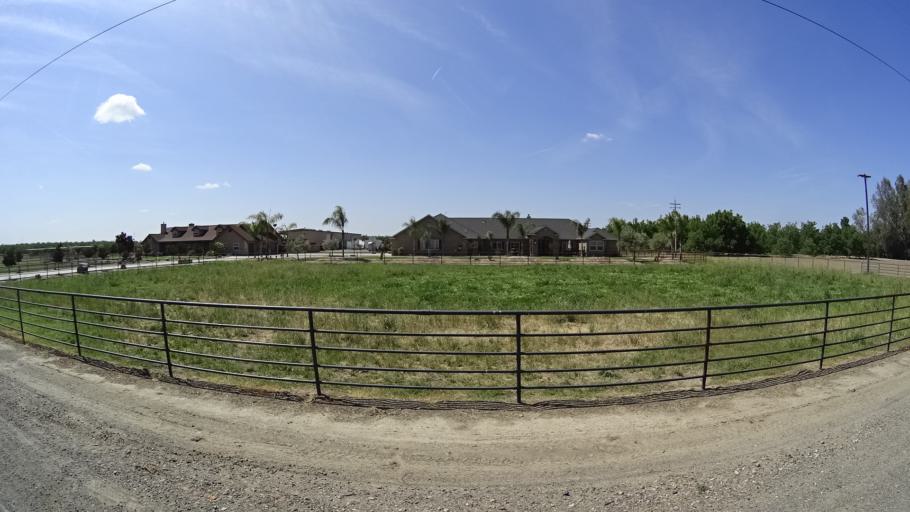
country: US
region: California
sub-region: Kings County
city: Armona
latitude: 36.2694
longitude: -119.7041
